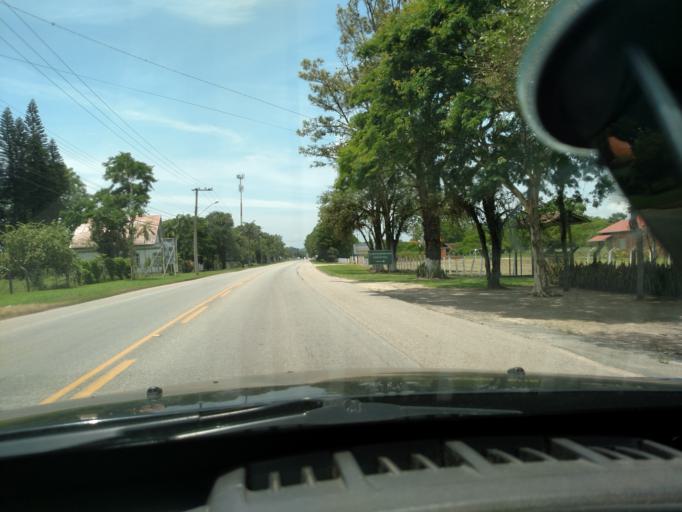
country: BR
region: Santa Catarina
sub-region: Gaspar
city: Gaspar
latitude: -26.9120
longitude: -48.9159
